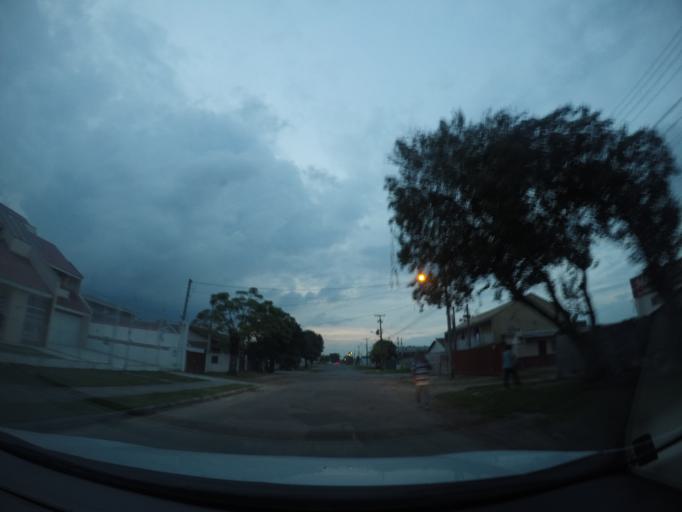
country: BR
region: Parana
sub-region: Sao Jose Dos Pinhais
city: Sao Jose dos Pinhais
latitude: -25.4994
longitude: -49.2303
